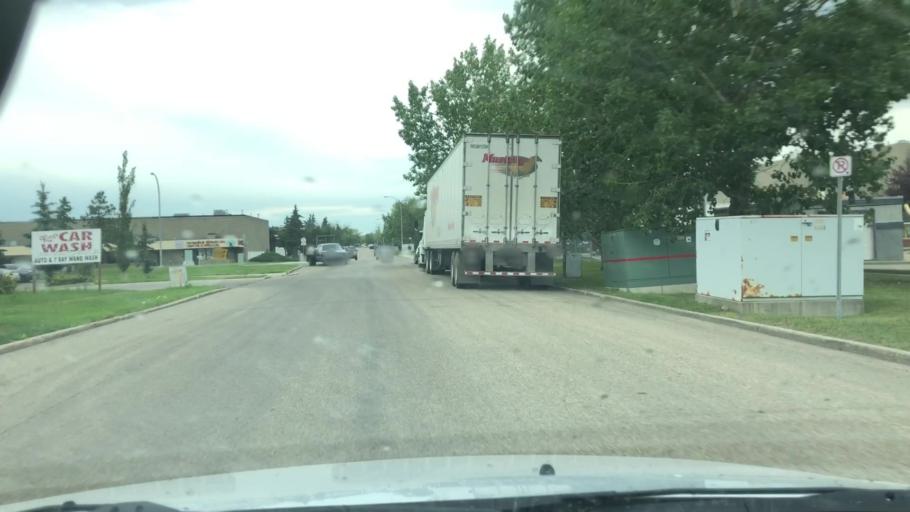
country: CA
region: Alberta
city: Edmonton
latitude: 53.5295
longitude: -113.4149
